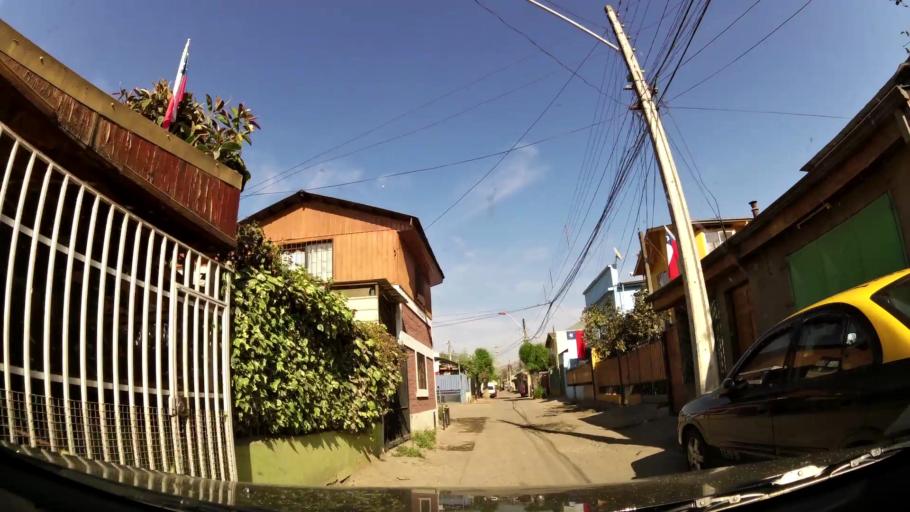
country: CL
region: Santiago Metropolitan
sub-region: Provincia de Santiago
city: Lo Prado
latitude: -33.3914
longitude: -70.6839
